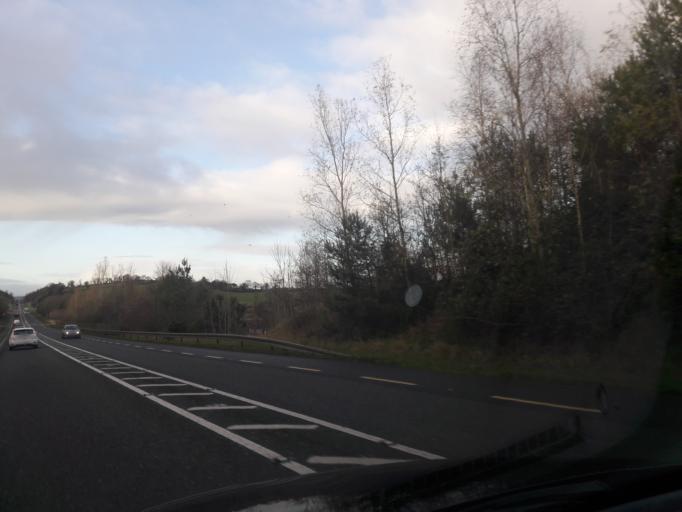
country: IE
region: Ulster
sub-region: County Monaghan
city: Carrickmacross
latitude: 53.9672
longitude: -6.6940
